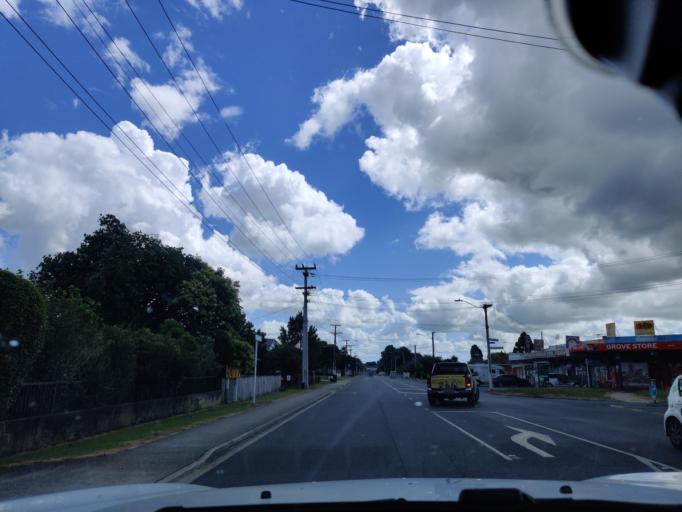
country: NZ
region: Auckland
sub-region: Auckland
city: Papakura
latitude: -37.0582
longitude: 174.9540
